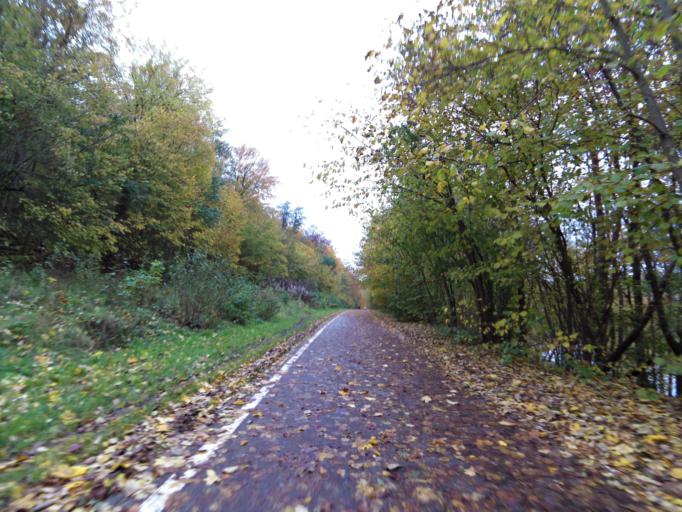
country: LT
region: Vilnius County
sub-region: Vilnius
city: Vilnius
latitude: 54.7295
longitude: 25.2989
